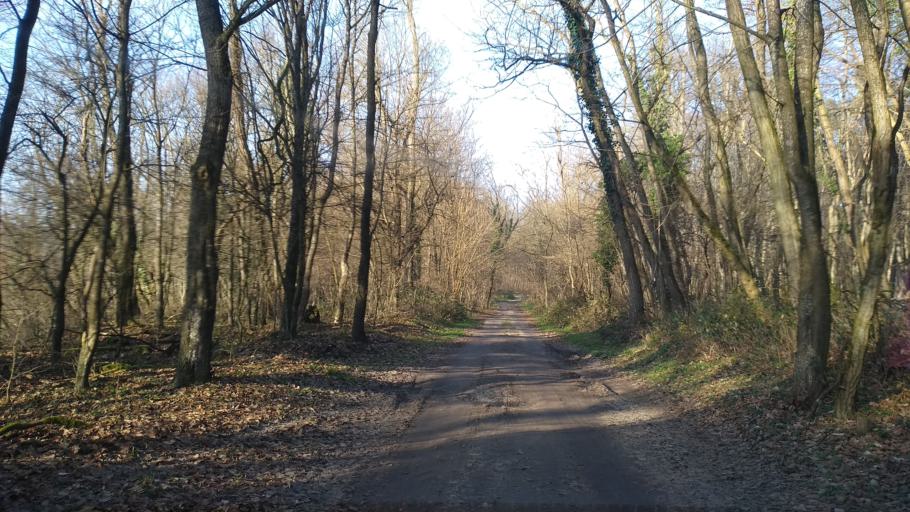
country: HU
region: Somogy
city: Barcs
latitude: 45.9509
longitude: 17.5214
